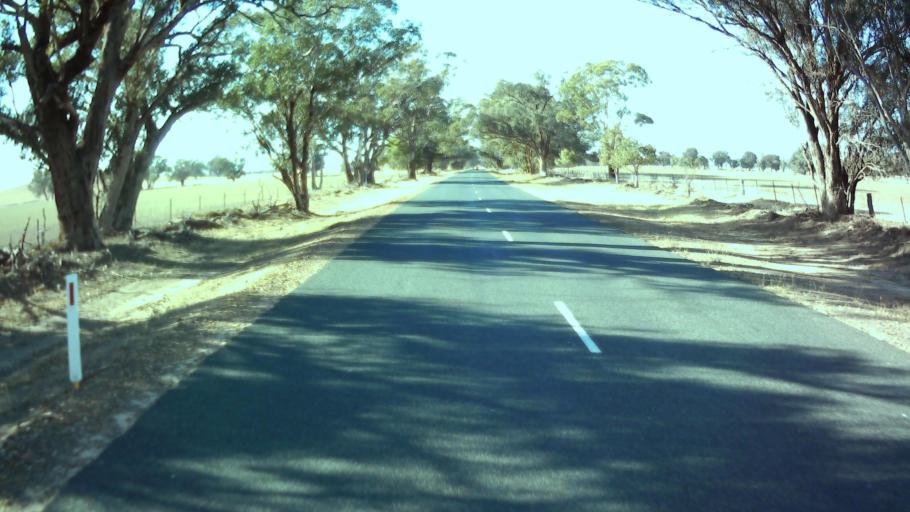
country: AU
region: New South Wales
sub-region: Weddin
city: Grenfell
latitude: -33.9578
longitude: 148.1396
